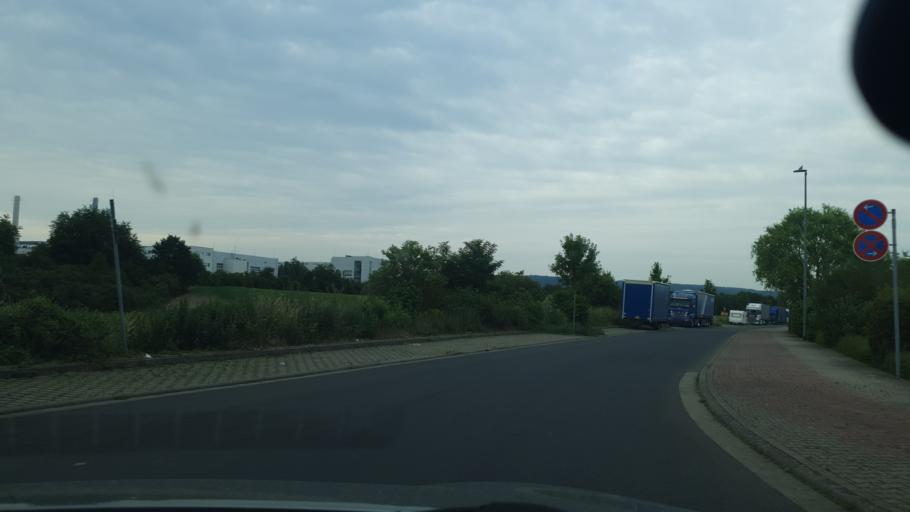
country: DE
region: Rheinland-Pfalz
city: Andernach
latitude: 50.4154
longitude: 7.4158
